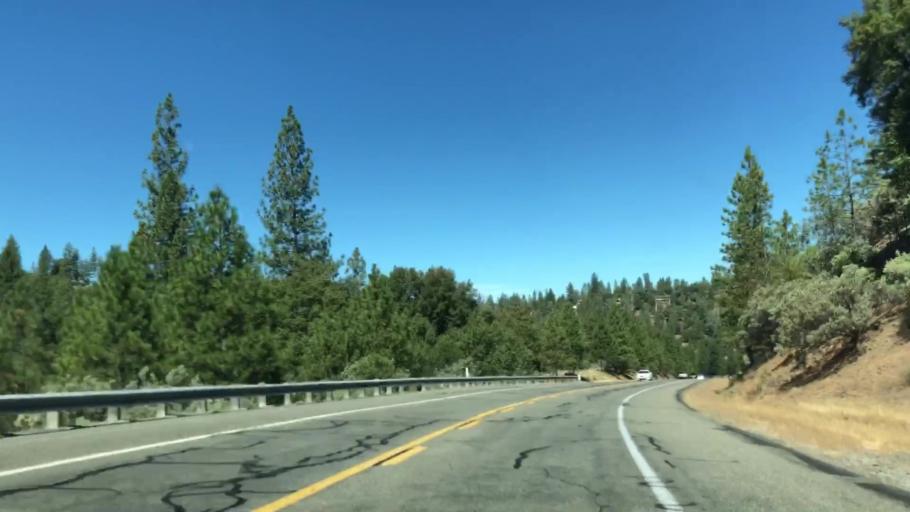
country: US
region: California
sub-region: Tuolumne County
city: Tuolumne City
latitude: 37.8341
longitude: -120.2030
